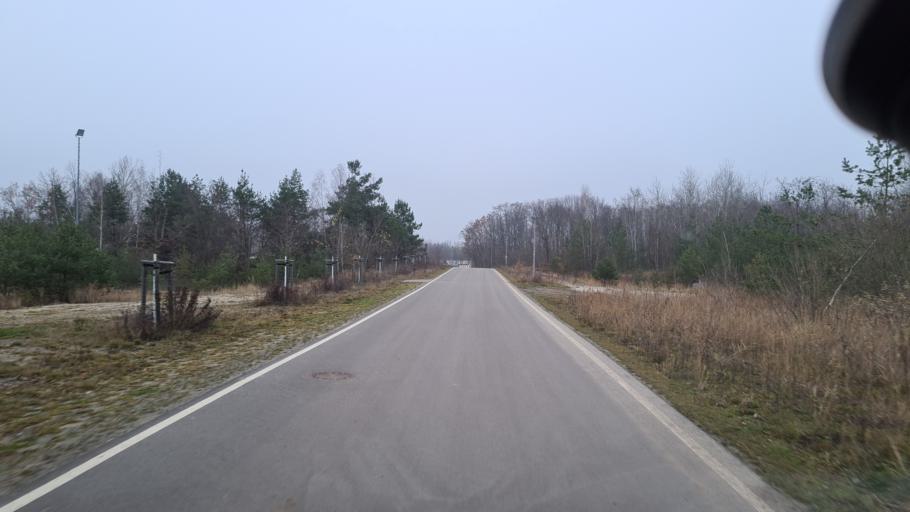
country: DE
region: Brandenburg
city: Sallgast
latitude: 51.5862
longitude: 13.7860
